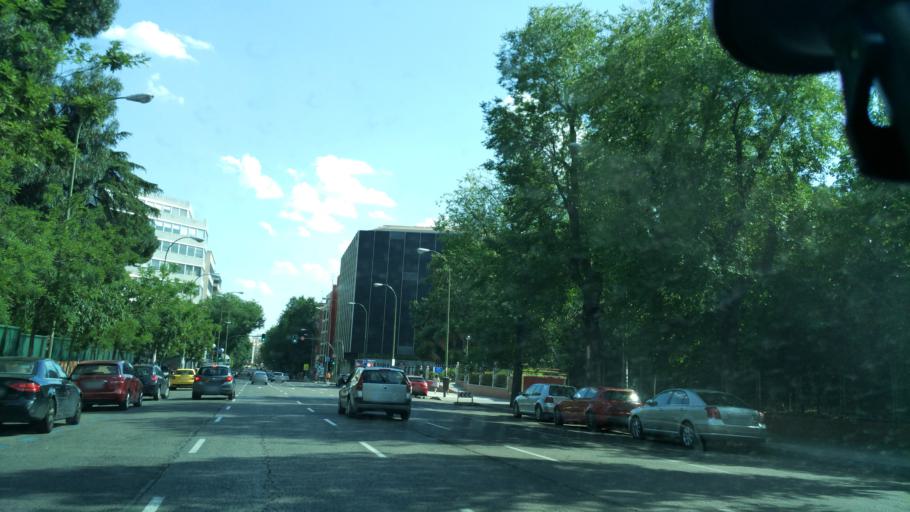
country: ES
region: Madrid
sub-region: Provincia de Madrid
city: Chamberi
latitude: 40.4400
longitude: -3.7042
